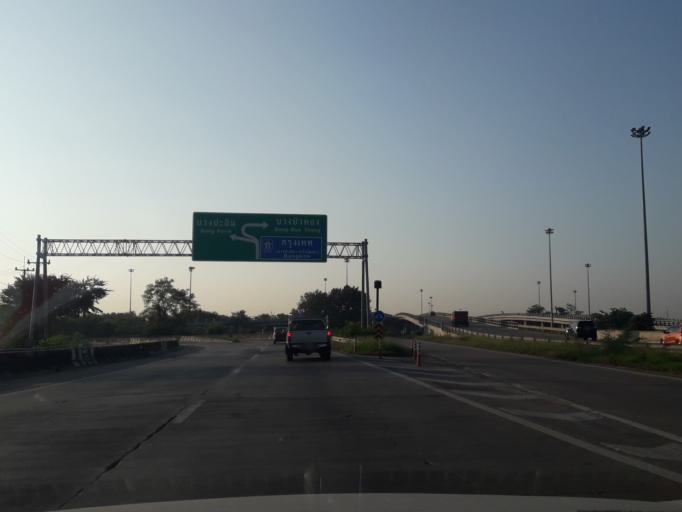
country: TH
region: Phra Nakhon Si Ayutthaya
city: Bang Pa-in
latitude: 14.1597
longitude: 100.5669
